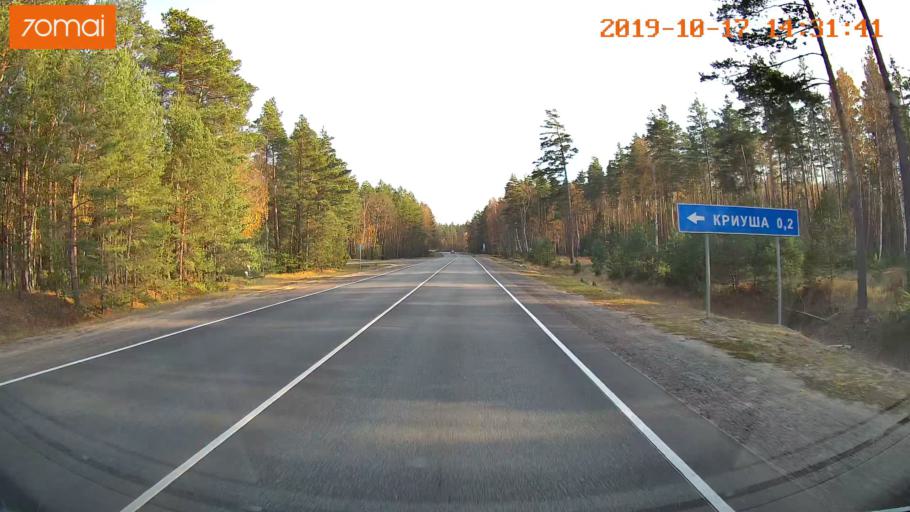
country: RU
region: Rjazan
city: Solotcha
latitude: 54.9342
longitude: 39.9685
